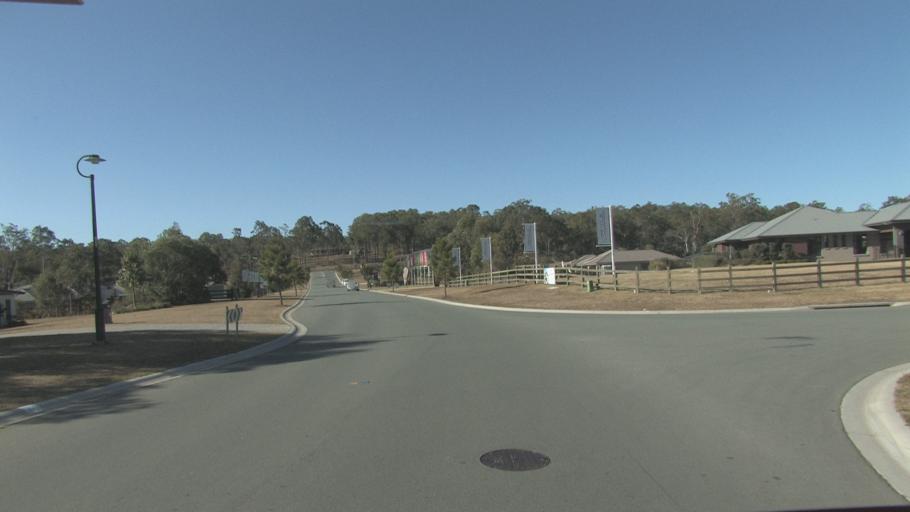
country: AU
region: Queensland
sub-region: Logan
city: Cedar Vale
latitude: -27.8667
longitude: 153.0569
